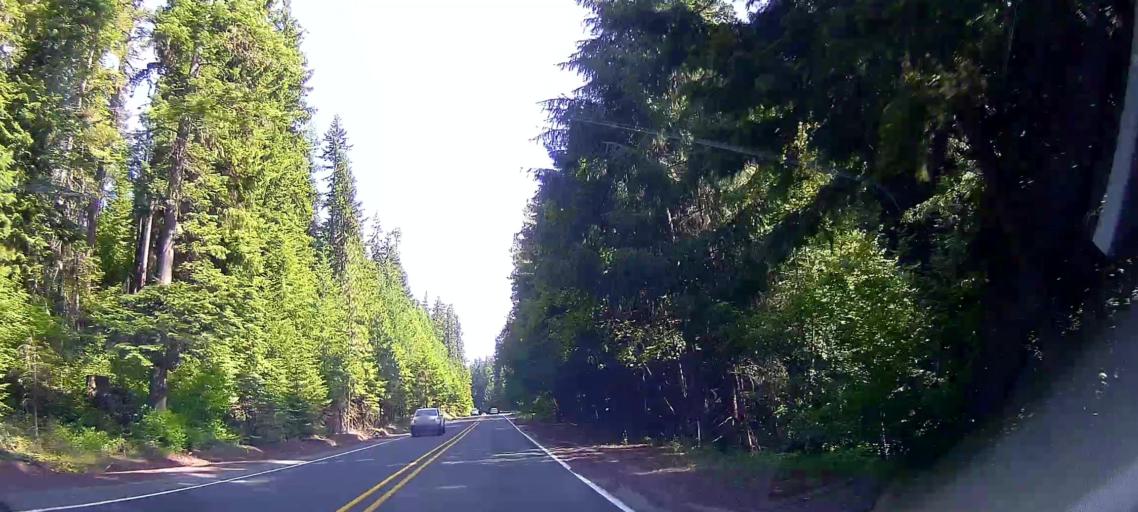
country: US
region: Oregon
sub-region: Jefferson County
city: Warm Springs
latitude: 45.0967
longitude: -121.5528
